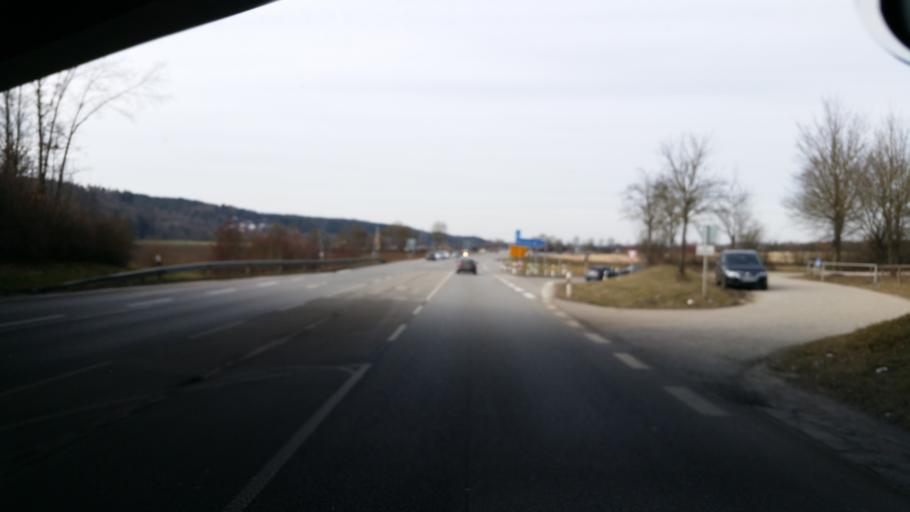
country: DE
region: Bavaria
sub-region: Lower Bavaria
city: Weihmichl
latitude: 48.5672
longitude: 12.0951
